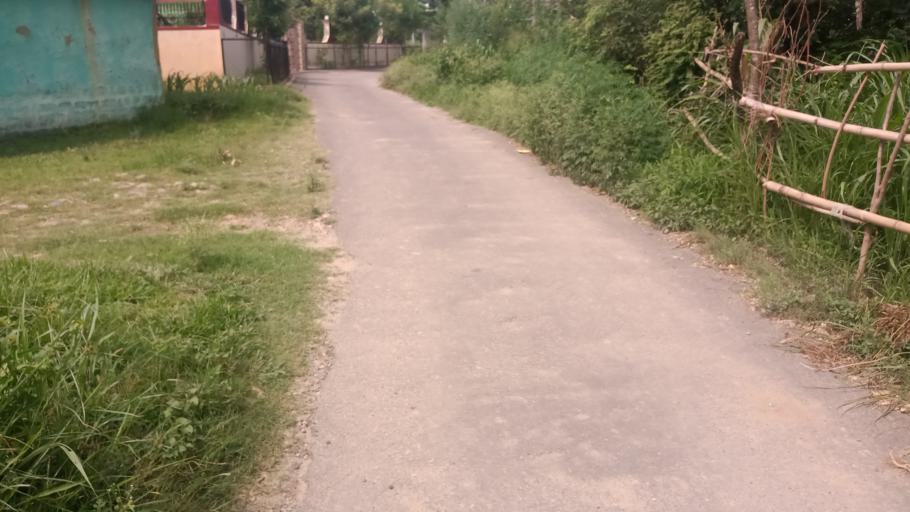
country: IN
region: Himachal Pradesh
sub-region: Hamirpur
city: Nadaun
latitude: 31.6928
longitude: 76.3574
